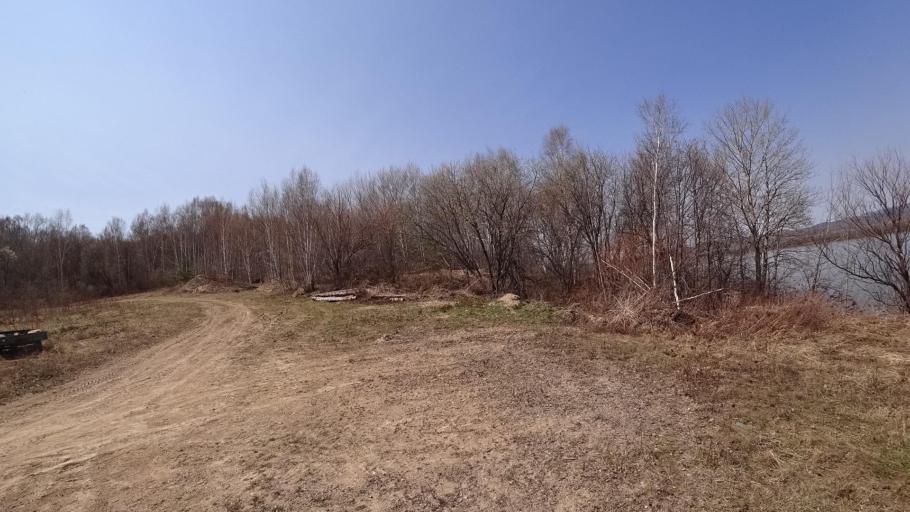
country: RU
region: Khabarovsk Krai
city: Selikhino
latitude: 50.6713
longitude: 137.3939
